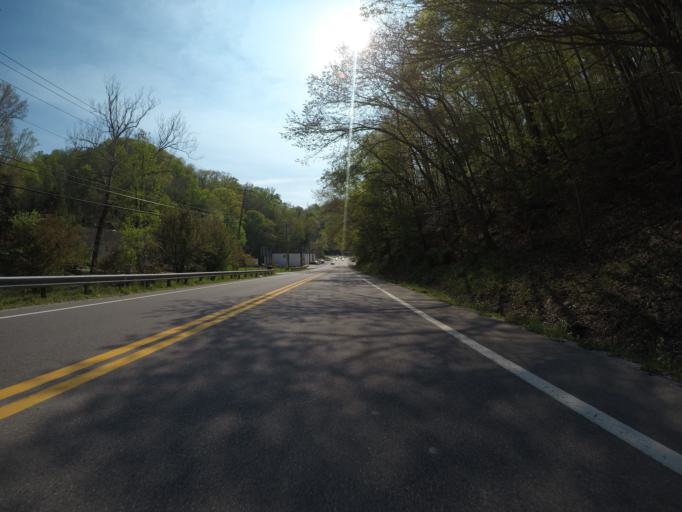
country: US
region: West Virginia
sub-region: Kanawha County
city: Charleston
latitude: 38.3594
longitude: -81.5908
